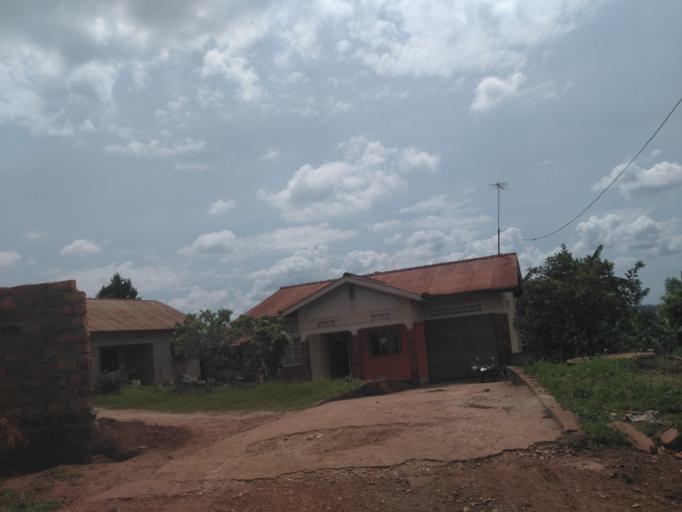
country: UG
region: Central Region
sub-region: Wakiso District
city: Bweyogerere
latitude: 0.4753
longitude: 32.6358
